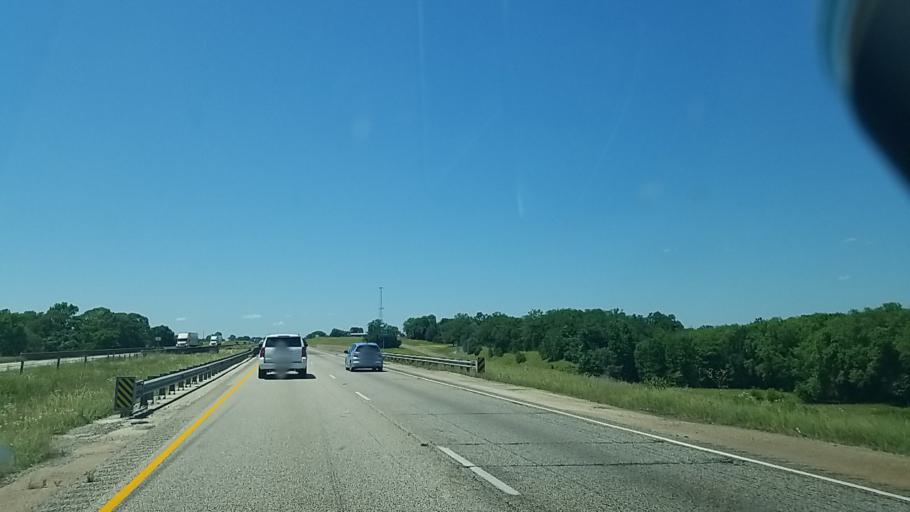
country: US
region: Texas
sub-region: Leon County
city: Buffalo
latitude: 31.4102
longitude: -96.0416
